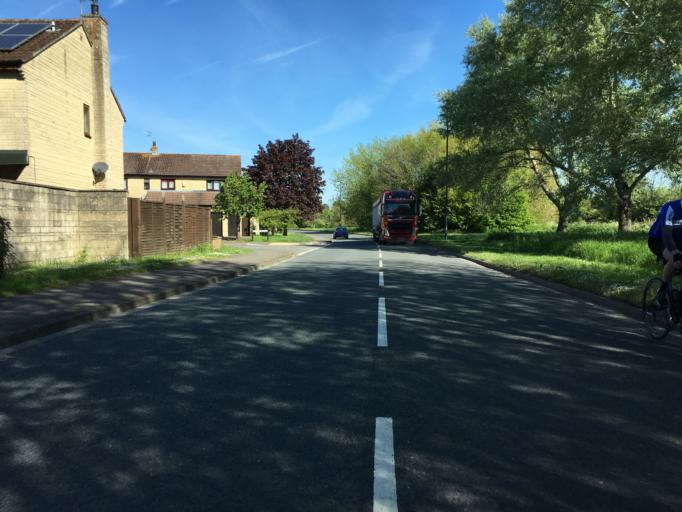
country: GB
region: England
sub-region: South Gloucestershire
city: Chipping Sodbury
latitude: 51.5408
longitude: -2.3845
